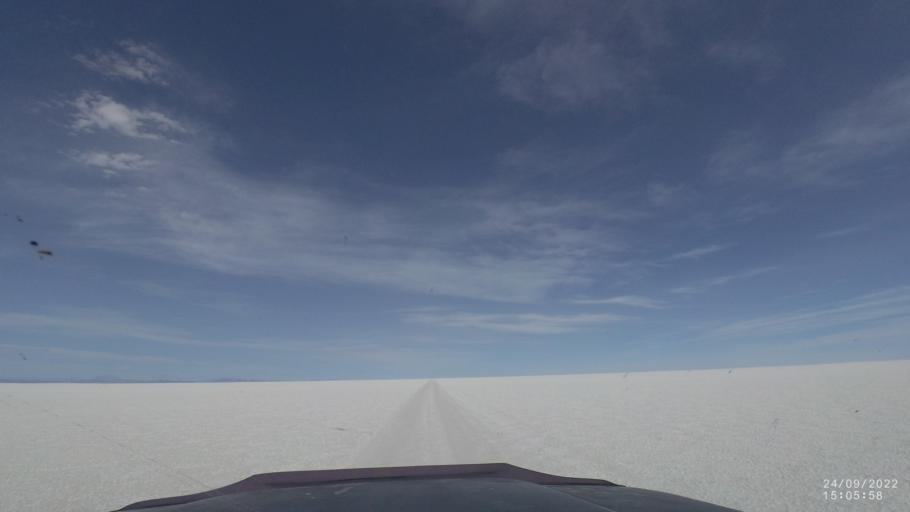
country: BO
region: Potosi
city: Colchani
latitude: -19.9098
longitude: -67.5135
